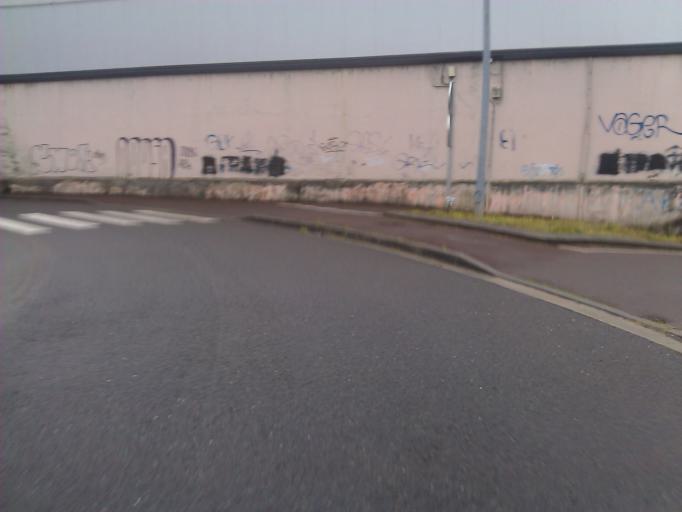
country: ES
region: Basque Country
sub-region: Provincia de Guipuzcoa
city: Hernani
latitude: 43.2718
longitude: -1.9645
